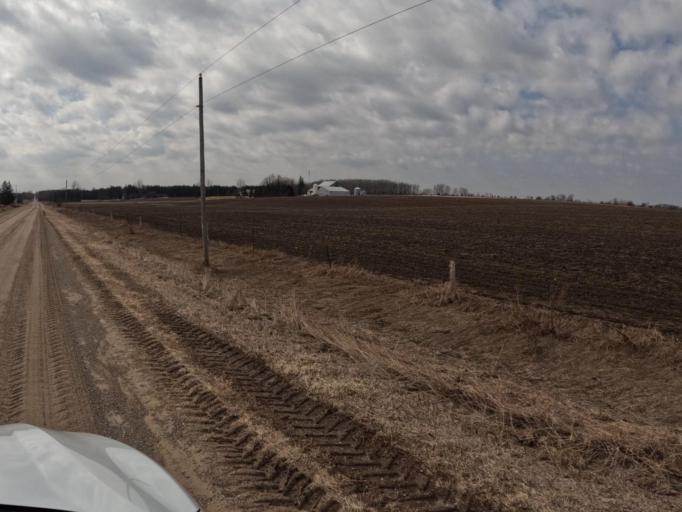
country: CA
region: Ontario
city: Orangeville
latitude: 43.9119
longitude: -80.2381
